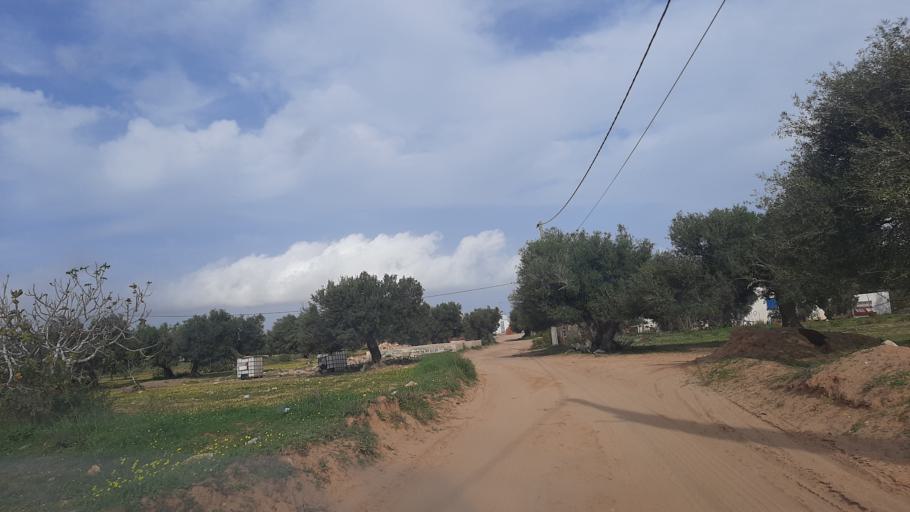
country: TN
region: Madanin
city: Midoun
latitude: 33.8057
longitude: 11.0244
